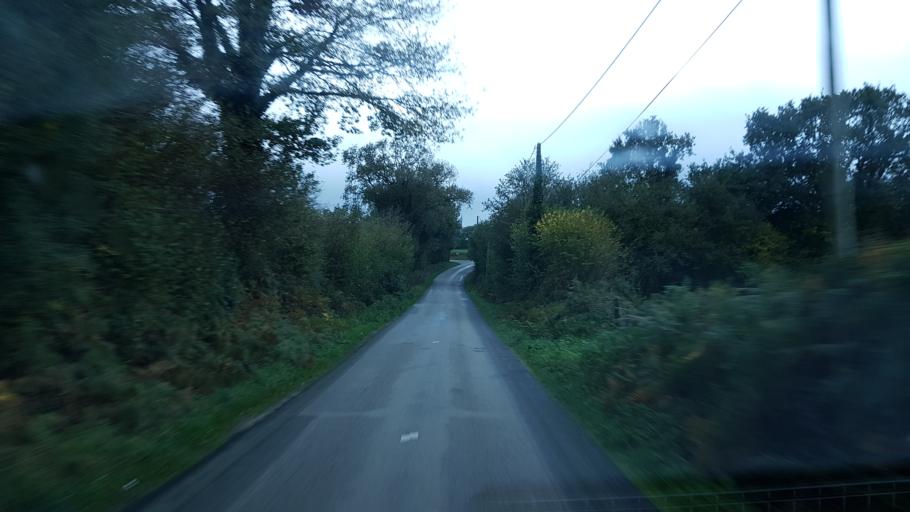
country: FR
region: Brittany
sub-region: Departement du Morbihan
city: Elven
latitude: 47.7111
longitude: -2.5861
